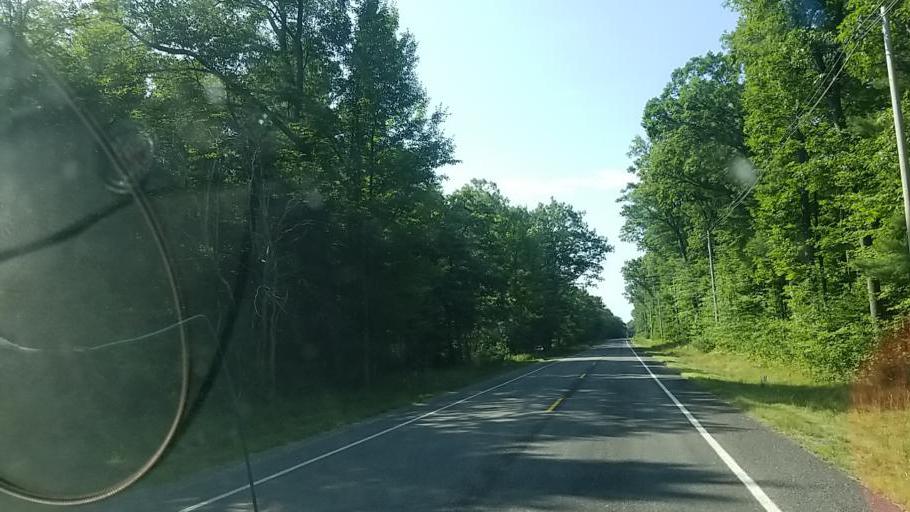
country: US
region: Michigan
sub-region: Muskegon County
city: Whitehall
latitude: 43.3521
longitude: -86.3764
